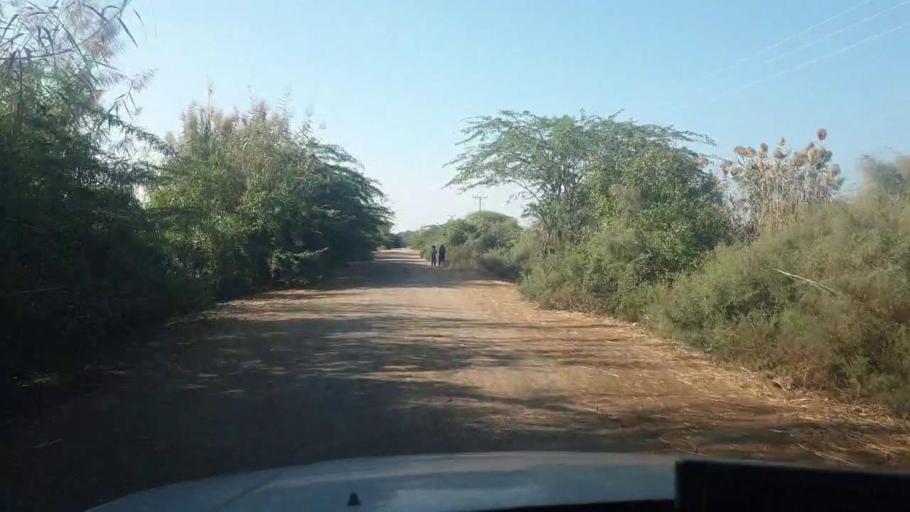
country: PK
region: Sindh
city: Mirpur Sakro
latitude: 24.4893
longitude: 67.6340
